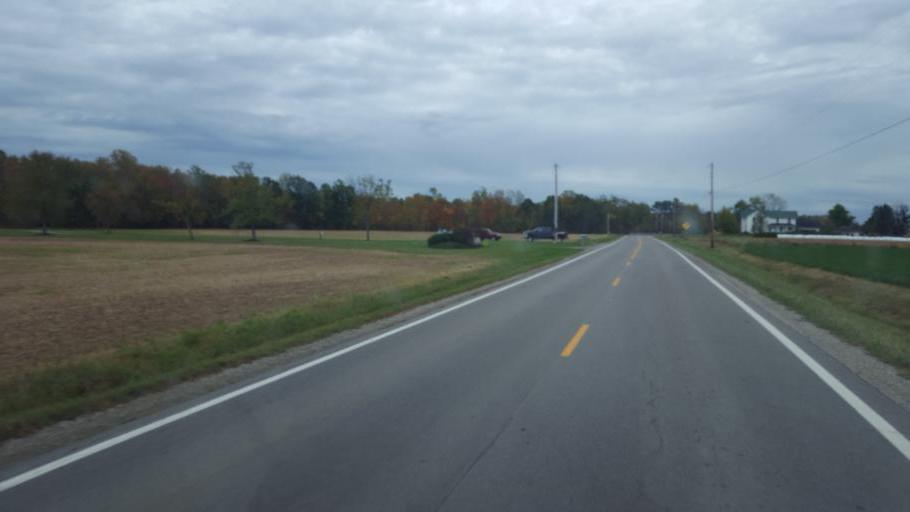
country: US
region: Ohio
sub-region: Huron County
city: Wakeman
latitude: 41.2375
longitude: -82.3942
